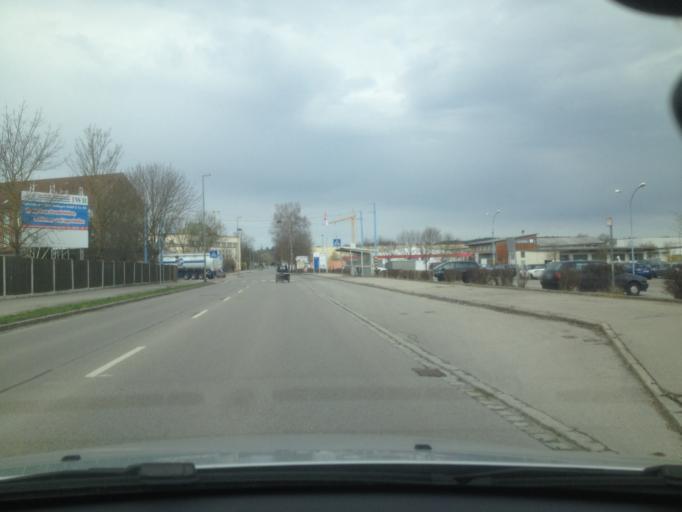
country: DE
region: Bavaria
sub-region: Swabia
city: Bobingen
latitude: 48.2648
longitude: 10.8165
